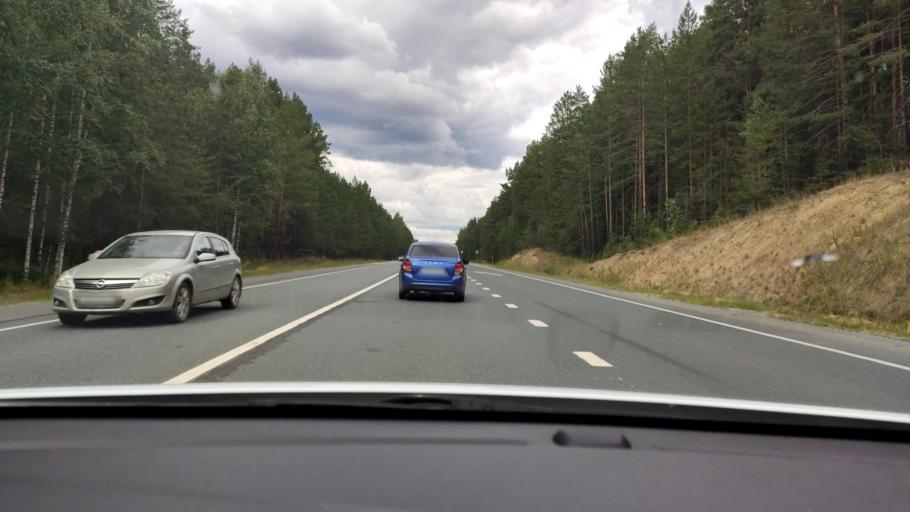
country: RU
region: Mariy-El
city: Pomary
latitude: 56.0614
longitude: 48.3700
